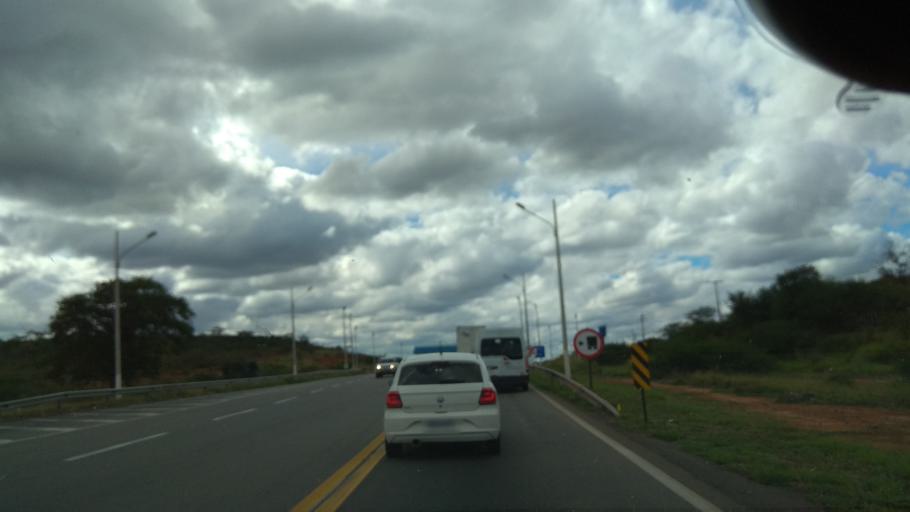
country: BR
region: Bahia
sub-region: Santa Ines
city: Santa Ines
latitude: -13.0110
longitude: -39.9575
